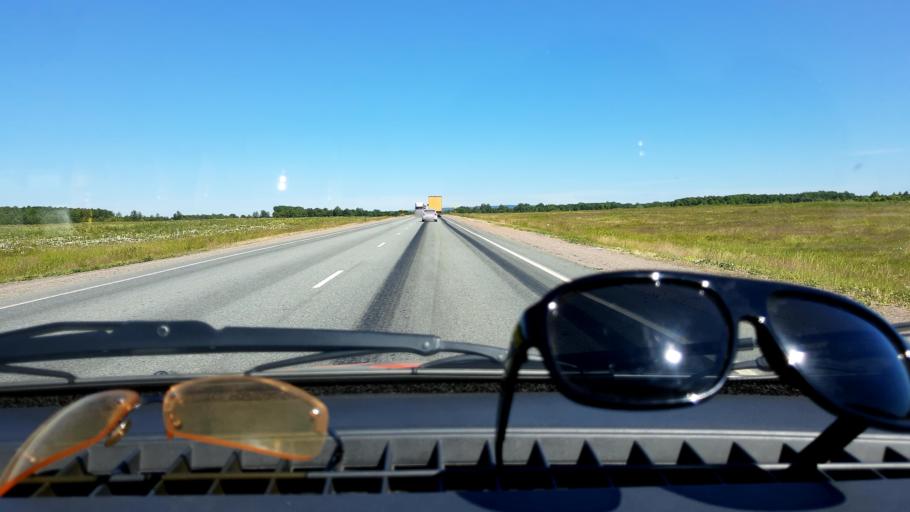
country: RU
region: Bashkortostan
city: Kudeyevskiy
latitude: 54.8171
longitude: 56.8106
